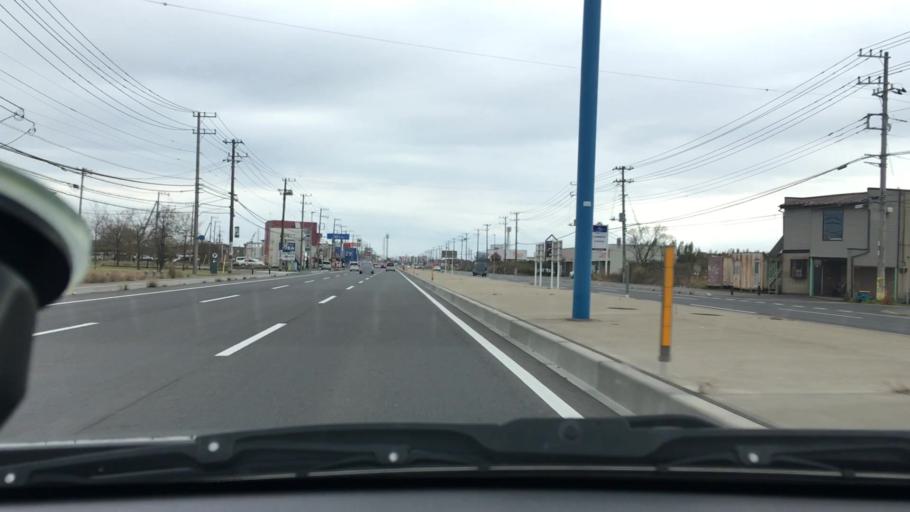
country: JP
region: Chiba
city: Omigawa
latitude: 35.8867
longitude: 140.6705
